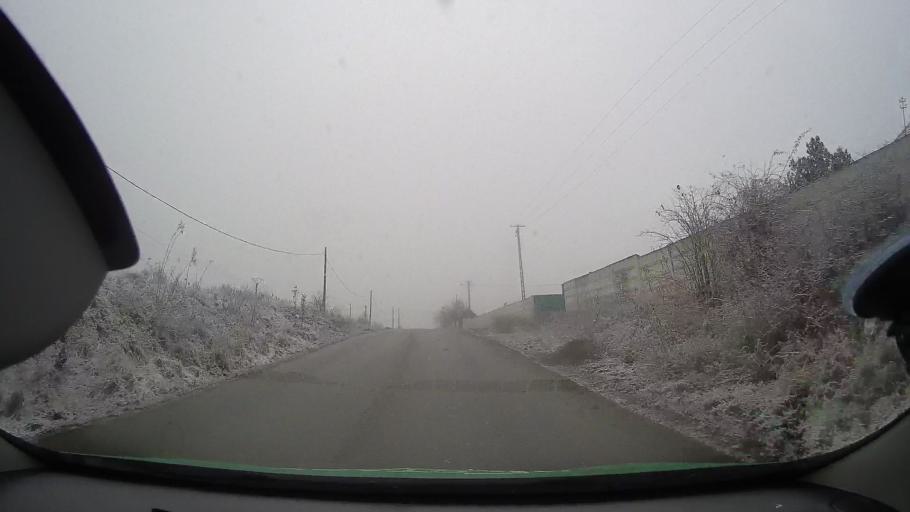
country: RO
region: Alba
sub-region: Comuna Noslac
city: Noslac
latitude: 46.3786
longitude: 23.9018
